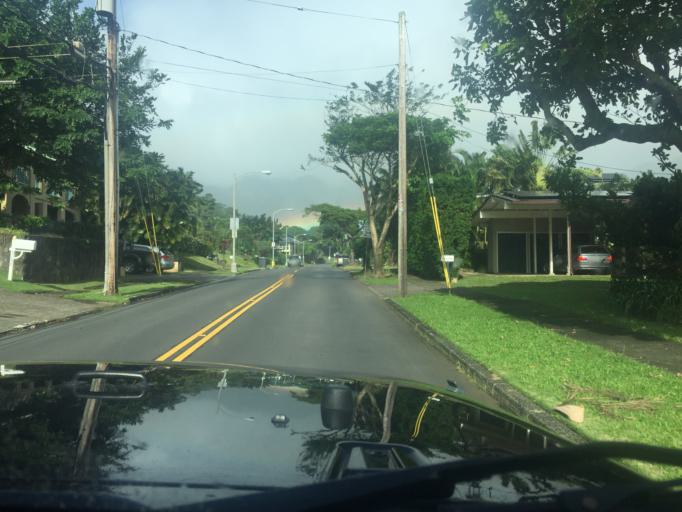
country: US
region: Hawaii
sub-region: Honolulu County
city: Honolulu
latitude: 21.3179
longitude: -157.8103
